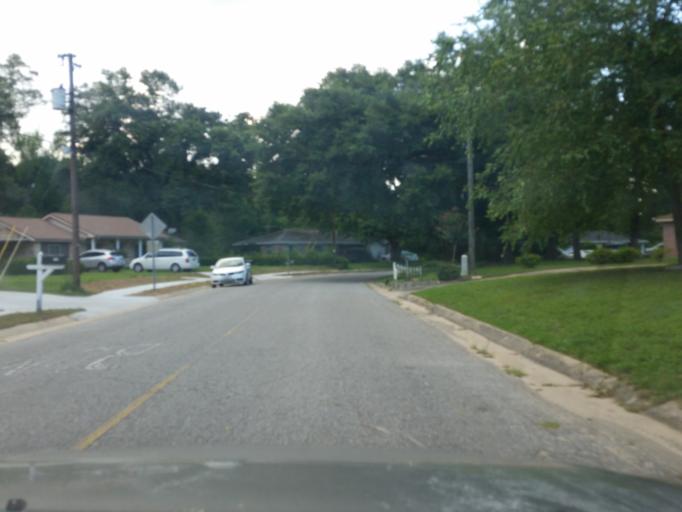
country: US
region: Florida
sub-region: Escambia County
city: Ferry Pass
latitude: 30.5113
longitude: -87.1955
